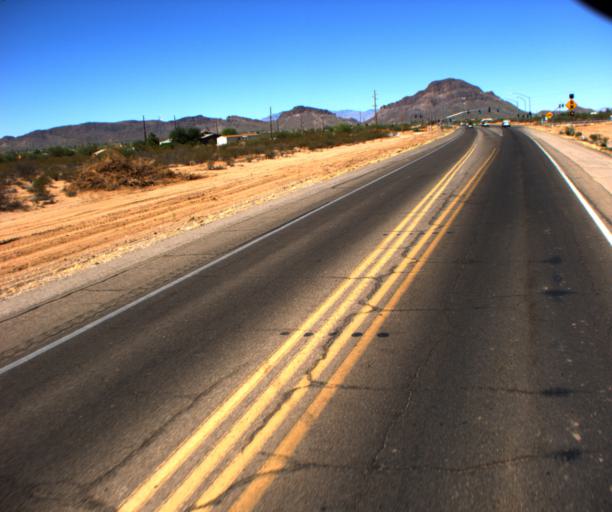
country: US
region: Arizona
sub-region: Pima County
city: Valencia West
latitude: 32.1577
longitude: -111.1083
